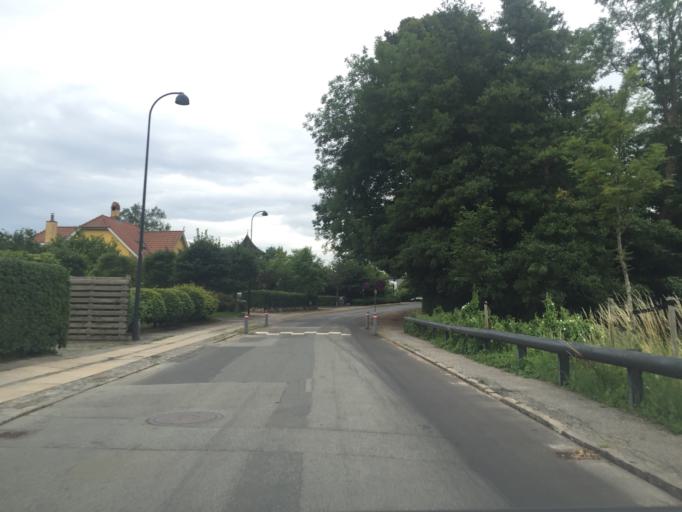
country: DK
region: Capital Region
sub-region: Lyngby-Tarbaek Kommune
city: Kongens Lyngby
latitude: 55.7650
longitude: 12.5362
